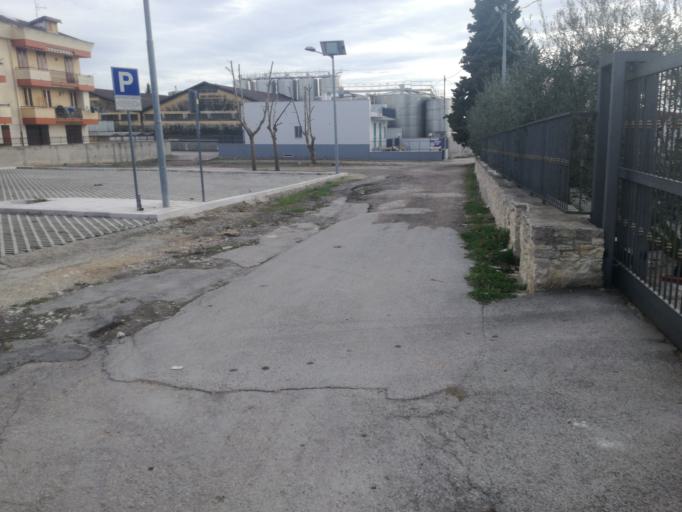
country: IT
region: Apulia
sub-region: Provincia di Bari
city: Ruvo di Puglia
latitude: 41.1192
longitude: 16.4763
